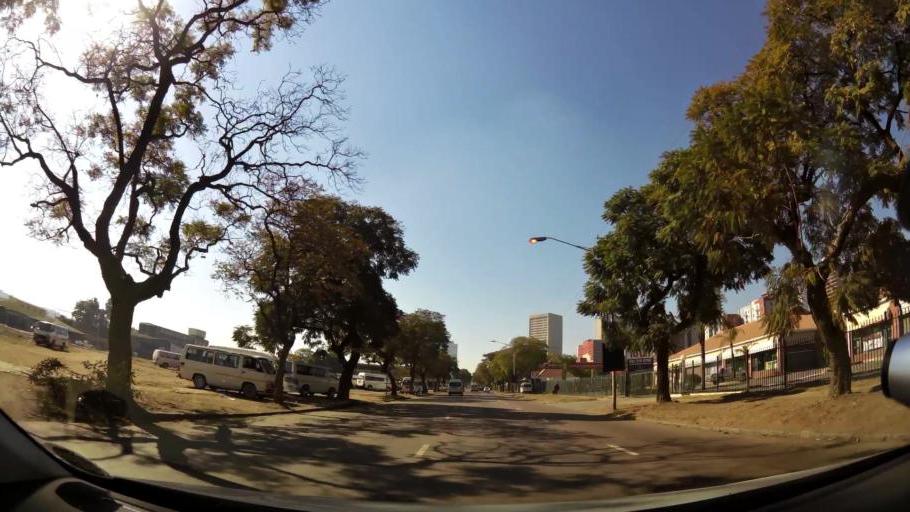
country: ZA
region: Gauteng
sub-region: City of Tshwane Metropolitan Municipality
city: Pretoria
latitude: -25.7426
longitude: 28.1790
